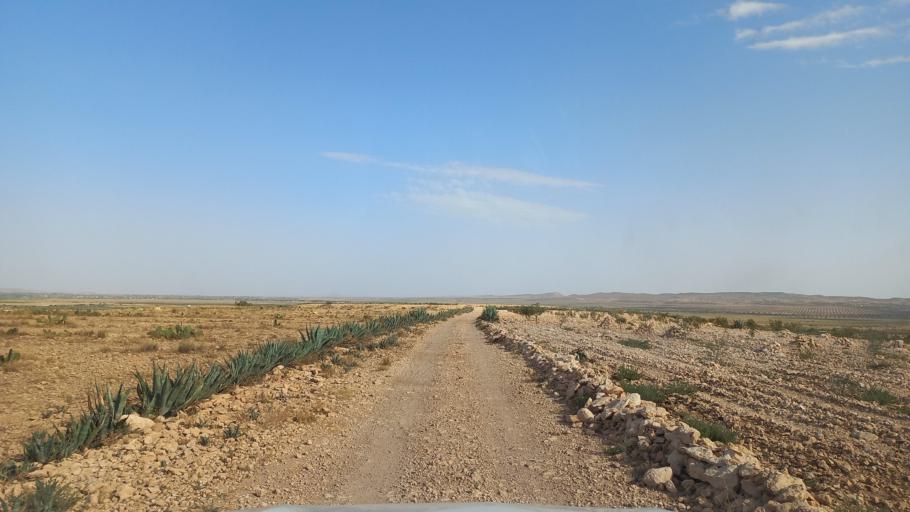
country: TN
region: Al Qasrayn
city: Kasserine
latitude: 35.2603
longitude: 8.9277
